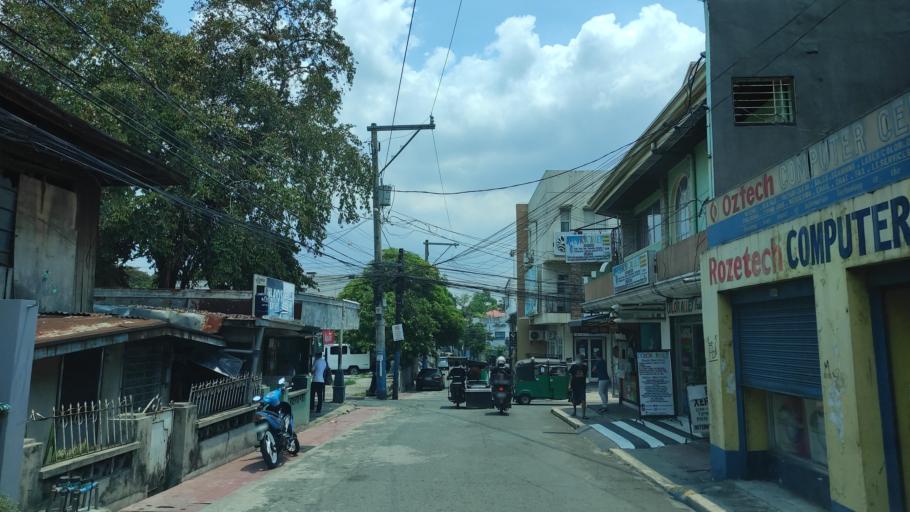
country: PH
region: Calabarzon
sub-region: Province of Rizal
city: Taytay
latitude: 14.5871
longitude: 121.1750
